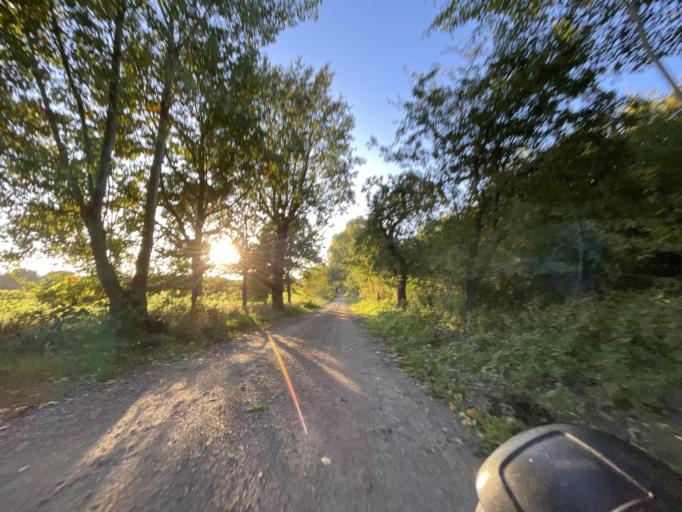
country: DE
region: Lower Saxony
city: Vastorf
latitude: 53.1992
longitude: 10.5370
